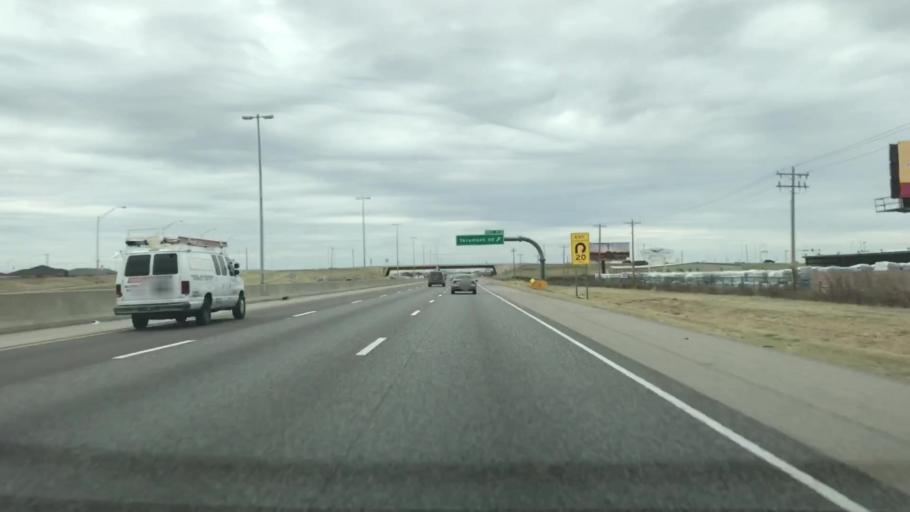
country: US
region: Oklahoma
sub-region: Cleveland County
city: Norman
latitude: 35.2579
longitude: -97.4854
